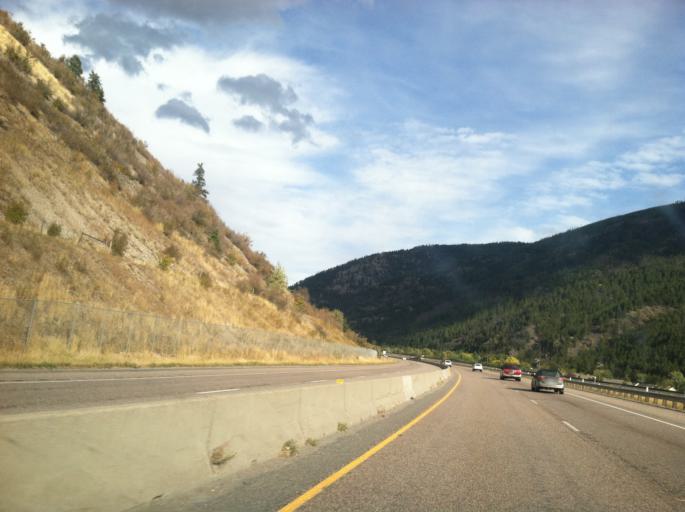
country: US
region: Montana
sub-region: Missoula County
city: East Missoula
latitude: 46.8633
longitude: -113.9675
